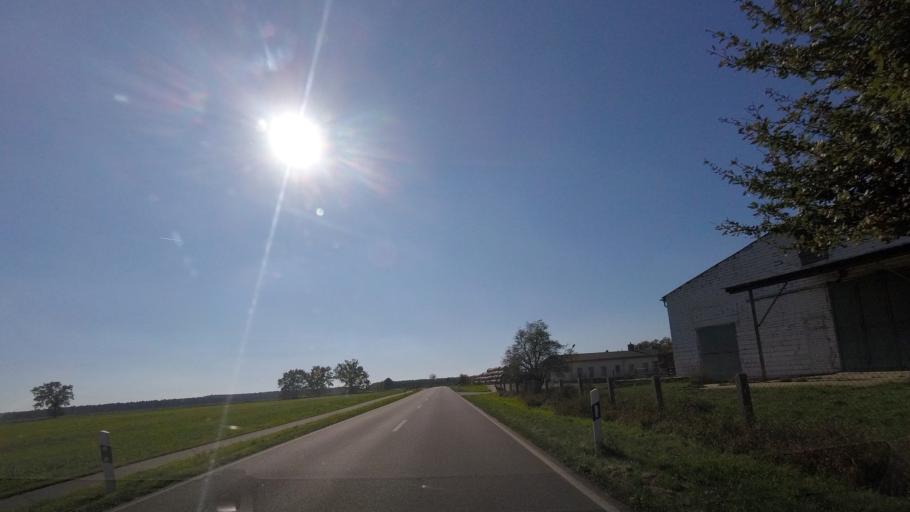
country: DE
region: Saxony-Anhalt
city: Muhlanger
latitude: 51.8649
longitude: 12.7826
